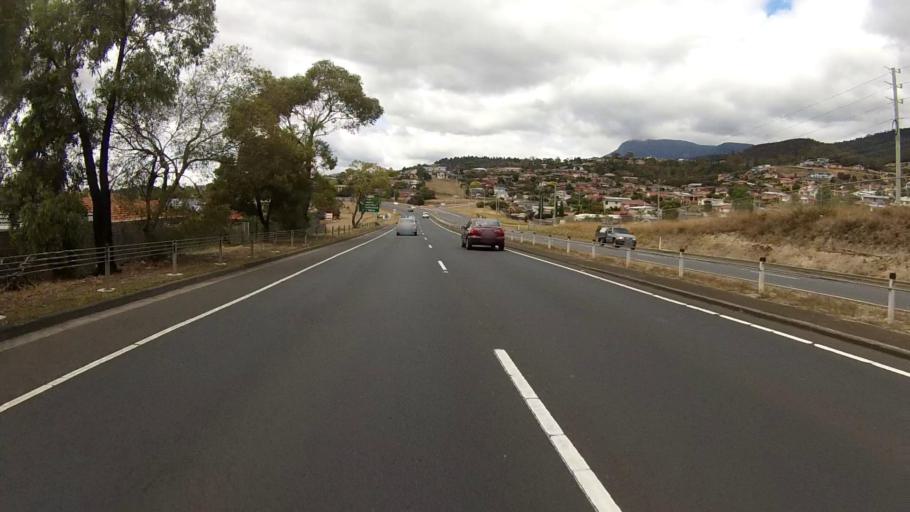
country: AU
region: Tasmania
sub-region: Glenorchy
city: Berriedale
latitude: -42.8121
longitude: 147.2507
